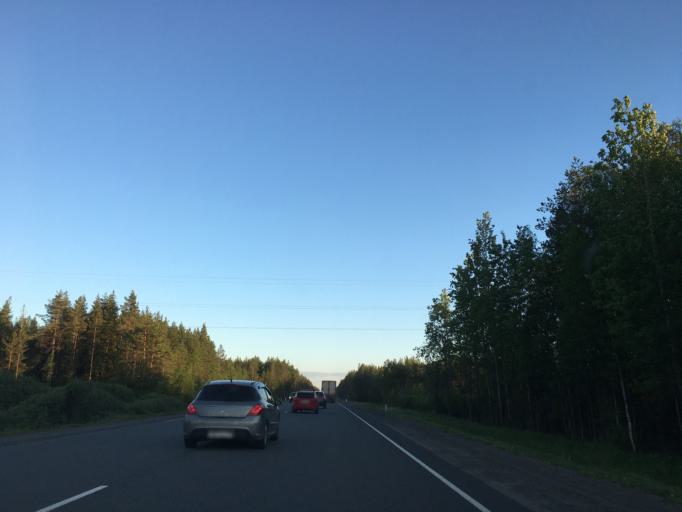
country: RU
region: Leningrad
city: Rozhdestveno
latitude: 59.2979
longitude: 29.9410
